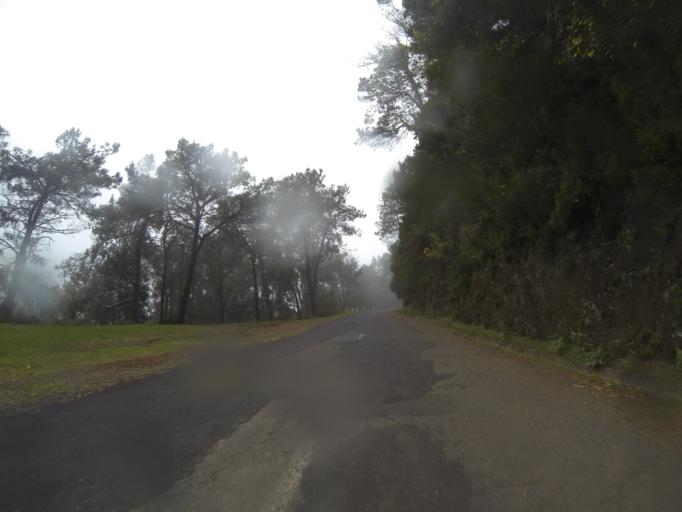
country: PT
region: Madeira
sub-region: Calheta
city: Estreito da Calheta
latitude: 32.7772
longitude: -17.1894
